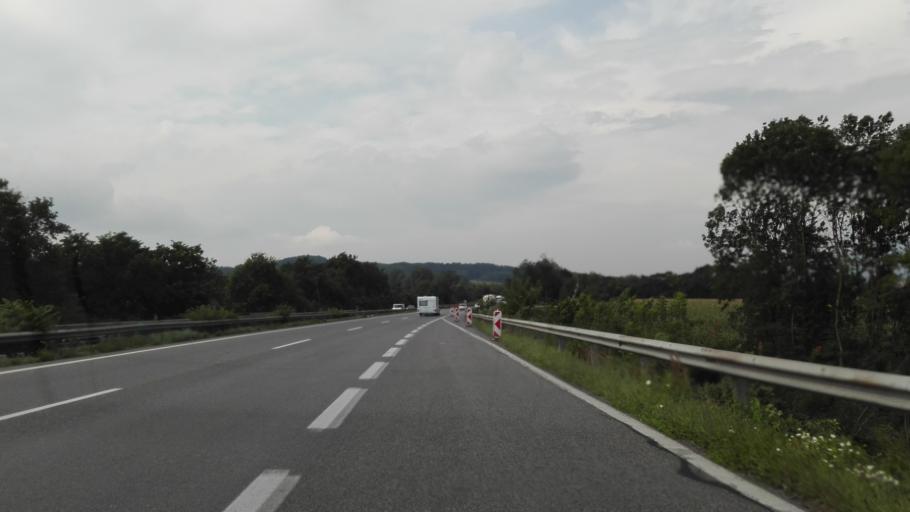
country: AT
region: Lower Austria
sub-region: Politischer Bezirk Melk
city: Klein-Poechlarn
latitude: 48.1979
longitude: 15.2519
